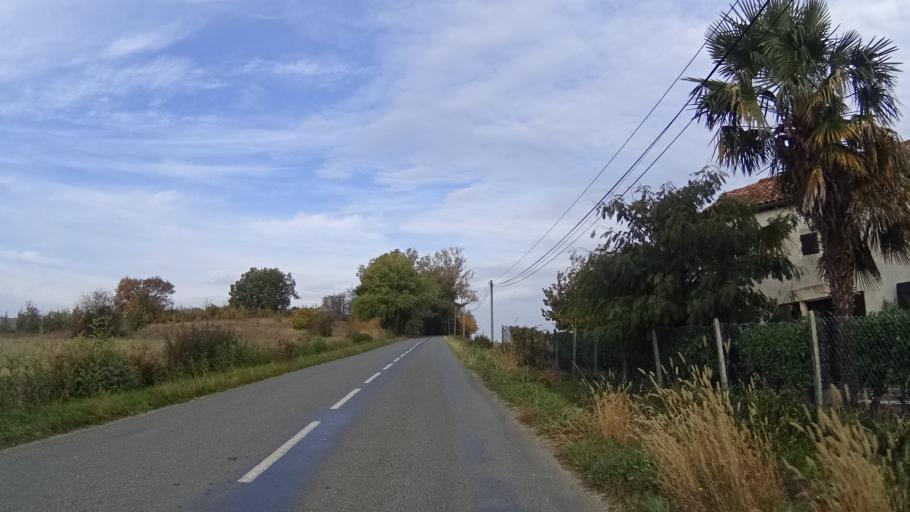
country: FR
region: Aquitaine
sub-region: Departement du Lot-et-Garonne
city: Laplume
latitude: 44.1067
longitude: 0.5473
